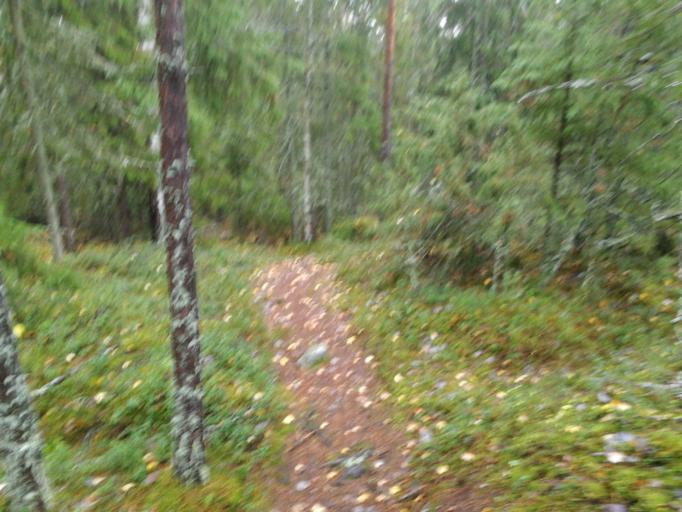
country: FI
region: Pirkanmaa
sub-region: Tampere
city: Tampere
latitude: 61.4565
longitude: 23.8782
